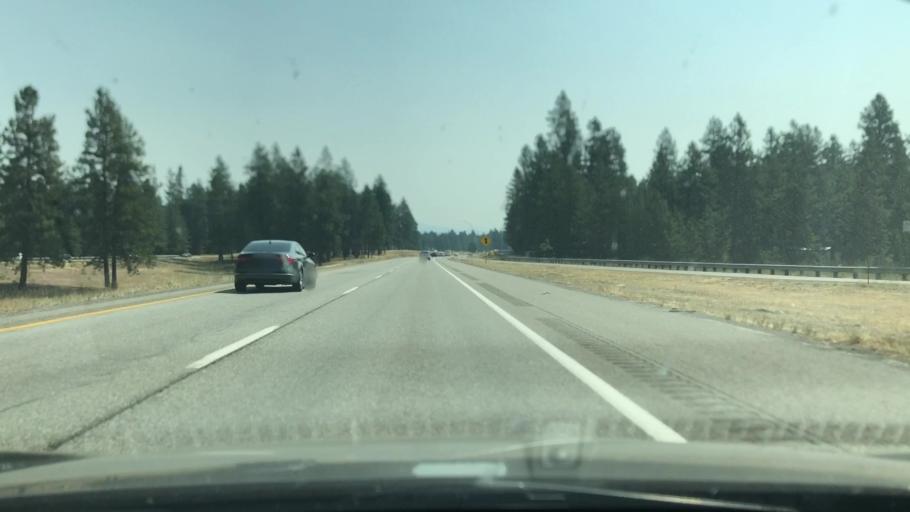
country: US
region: Idaho
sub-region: Kootenai County
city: Coeur d'Alene
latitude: 47.7085
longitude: -116.8621
